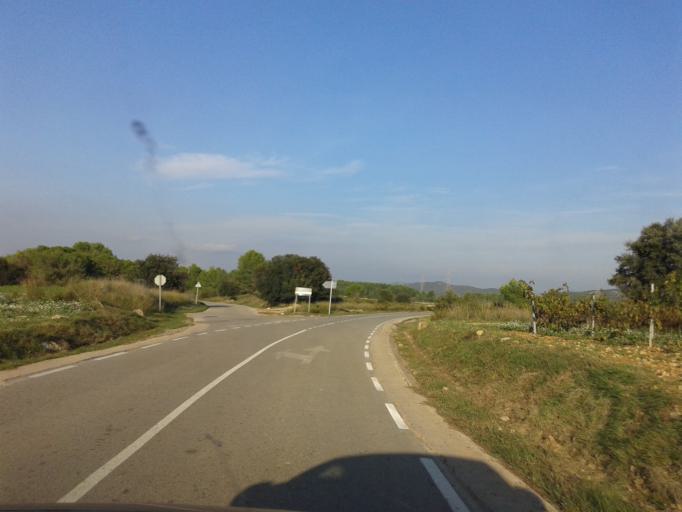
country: ES
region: Catalonia
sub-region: Provincia de Barcelona
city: Vilafranca del Penedes
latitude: 41.3235
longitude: 1.7041
